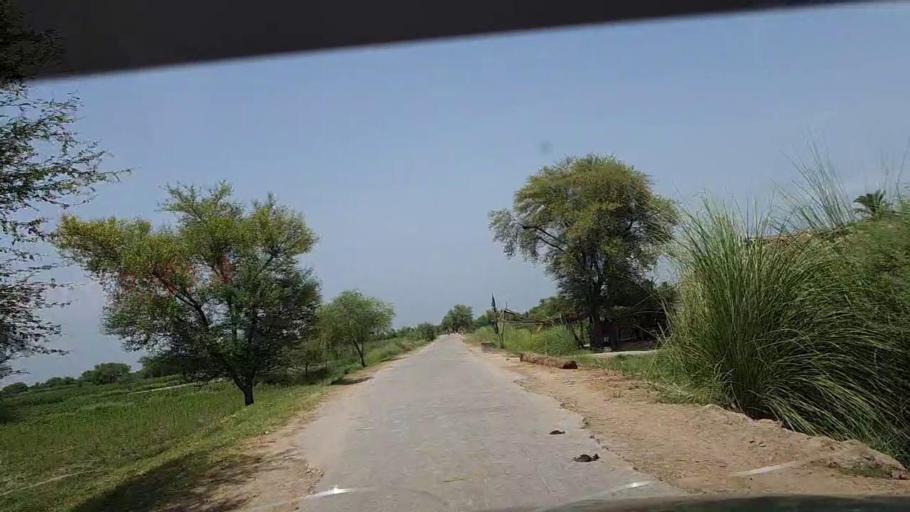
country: PK
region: Sindh
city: Khanpur
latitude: 27.8010
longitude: 69.4509
